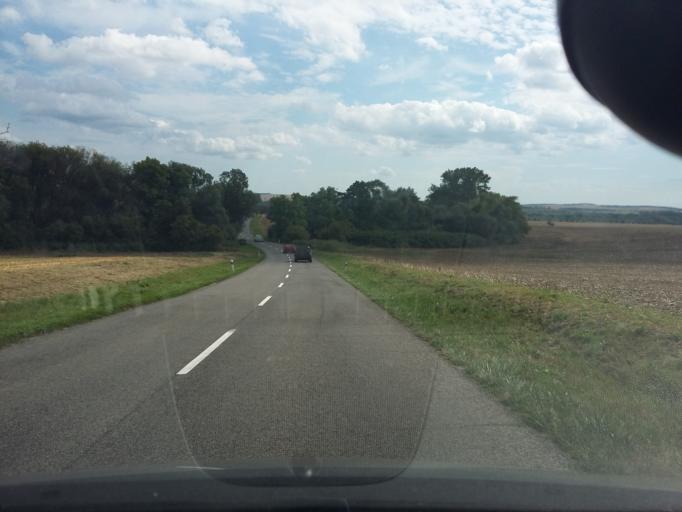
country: SK
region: Trnavsky
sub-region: Okres Skalica
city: Holic
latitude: 48.7518
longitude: 17.1705
